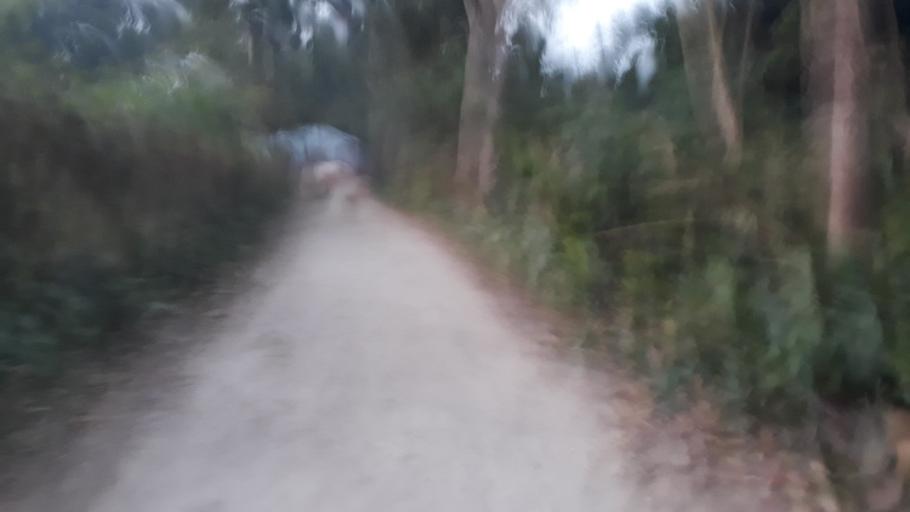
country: BD
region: Khulna
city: Kaliganj
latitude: 23.3497
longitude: 88.9074
